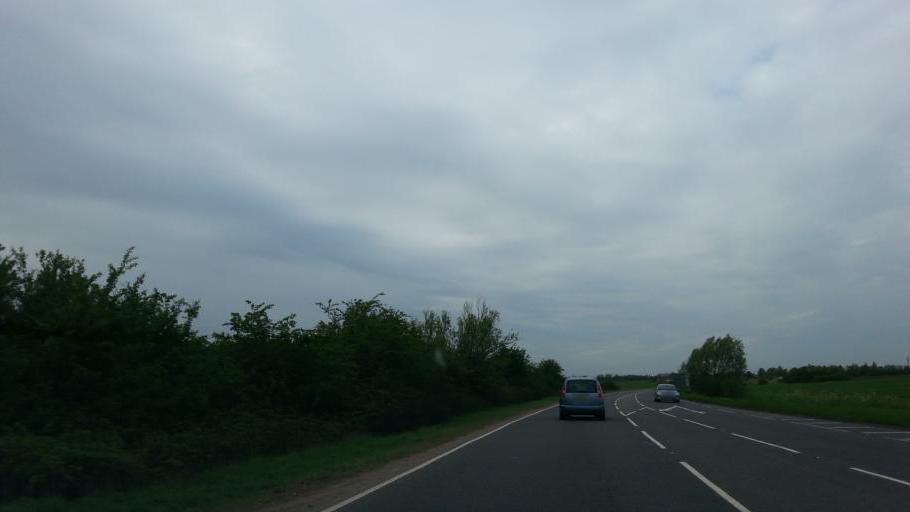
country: GB
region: England
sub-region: Cambridgeshire
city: March
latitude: 52.5343
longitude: 0.0693
